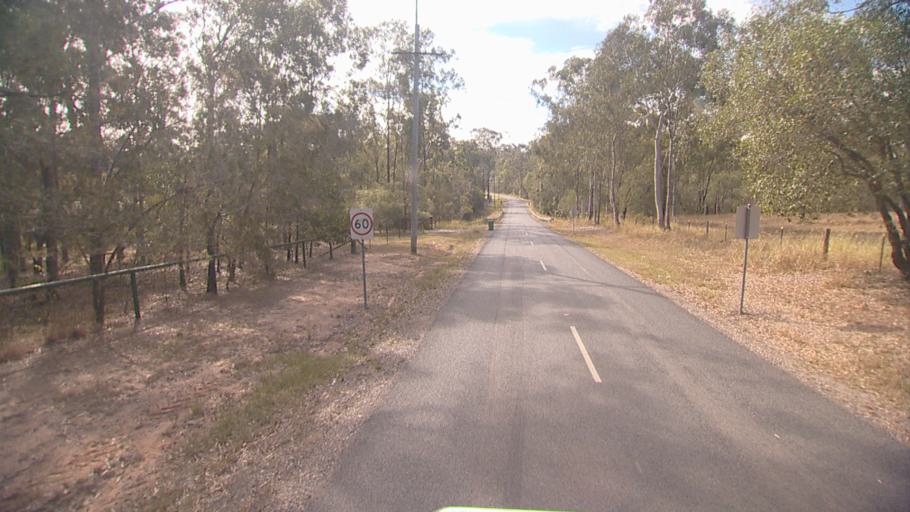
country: AU
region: Queensland
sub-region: Logan
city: North Maclean
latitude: -27.7587
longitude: 152.9721
